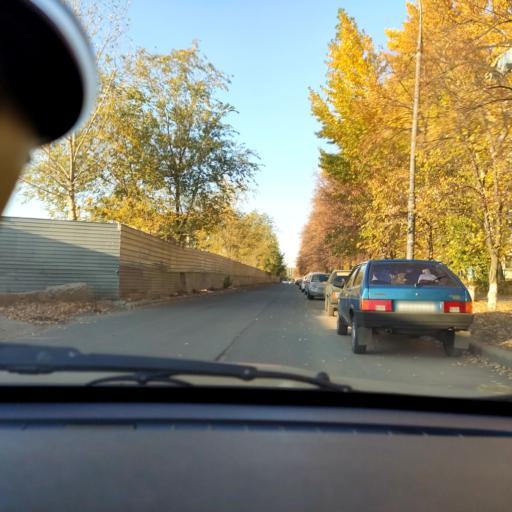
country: RU
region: Samara
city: Tol'yatti
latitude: 53.5309
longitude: 49.2831
